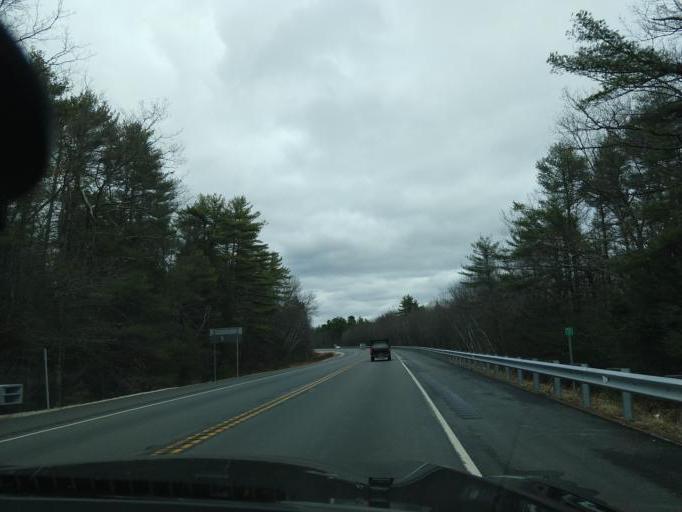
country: US
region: New Hampshire
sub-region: Rockingham County
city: Kingston
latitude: 42.9205
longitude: -71.0486
